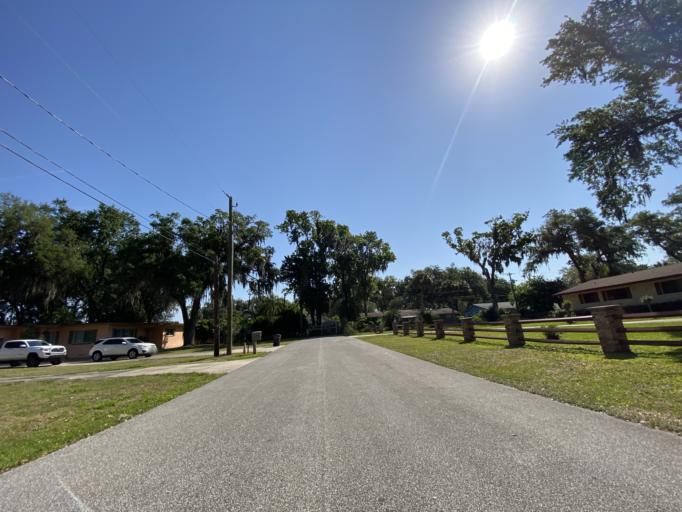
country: US
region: Florida
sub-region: Volusia County
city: South Daytona
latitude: 29.1681
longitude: -81.0153
